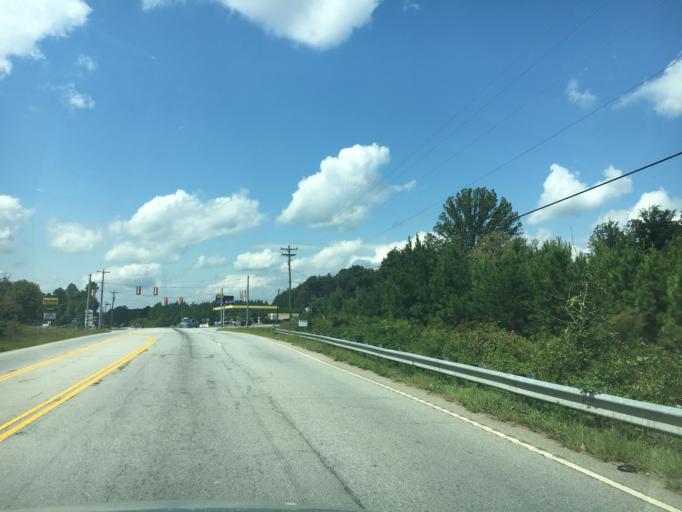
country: US
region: South Carolina
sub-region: Greenville County
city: Berea
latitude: 34.8906
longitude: -82.5323
